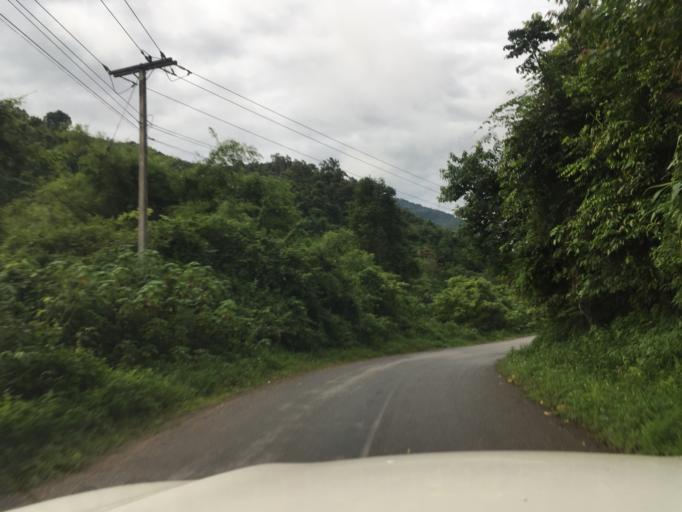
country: LA
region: Oudomxai
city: Muang La
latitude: 21.0590
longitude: 102.2415
